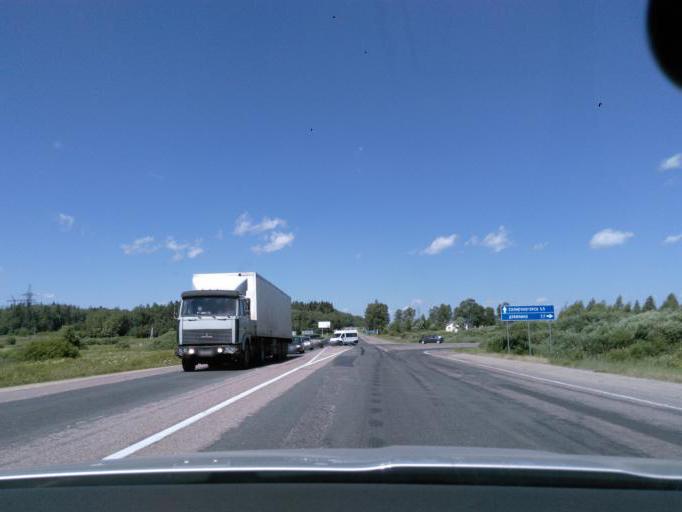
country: RU
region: Moskovskaya
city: Solnechnogorsk
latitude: 56.1535
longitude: 36.9197
